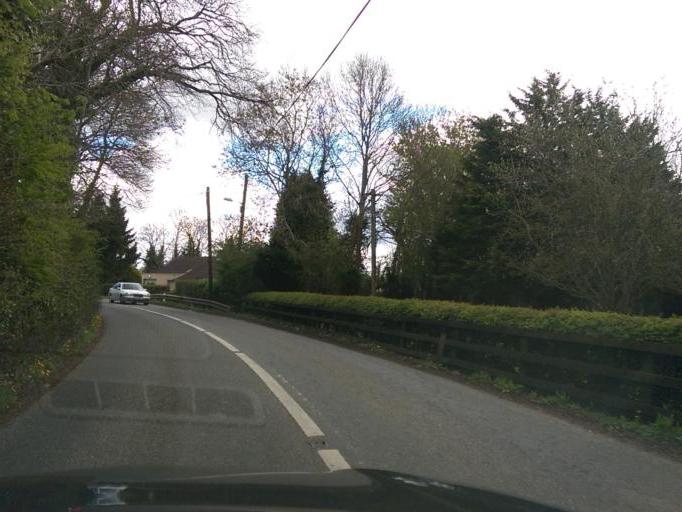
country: IE
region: Leinster
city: Lucan
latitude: 53.3726
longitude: -6.4637
